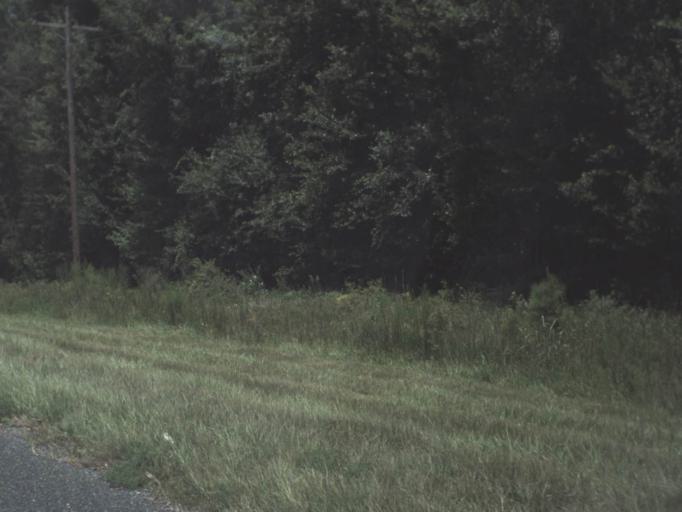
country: US
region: Florida
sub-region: Taylor County
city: Perry
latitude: 29.9692
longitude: -83.4779
